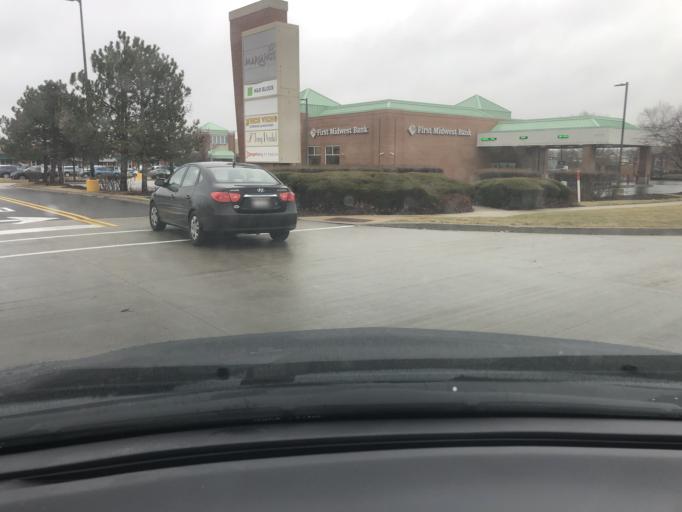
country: US
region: Illinois
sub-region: Will County
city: Shorewood
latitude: 41.5380
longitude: -88.1993
